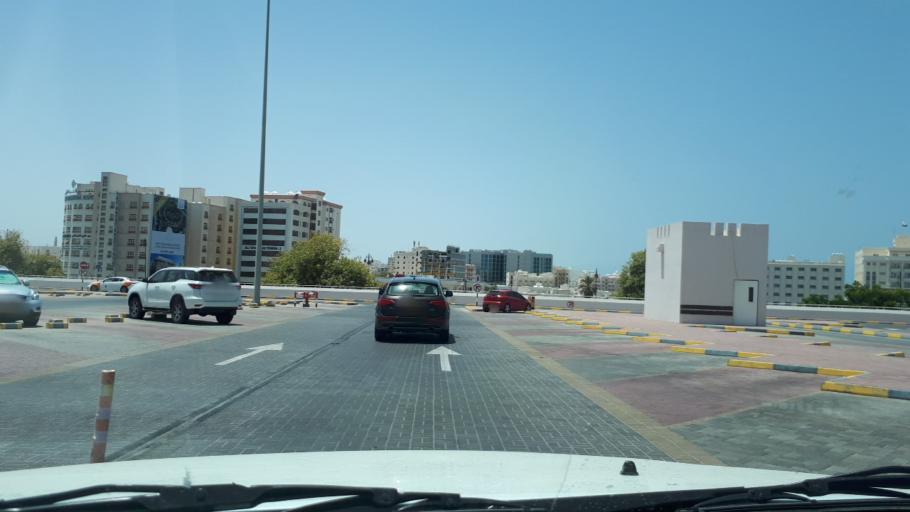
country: OM
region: Muhafazat Masqat
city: Bawshar
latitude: 23.5903
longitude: 58.4096
